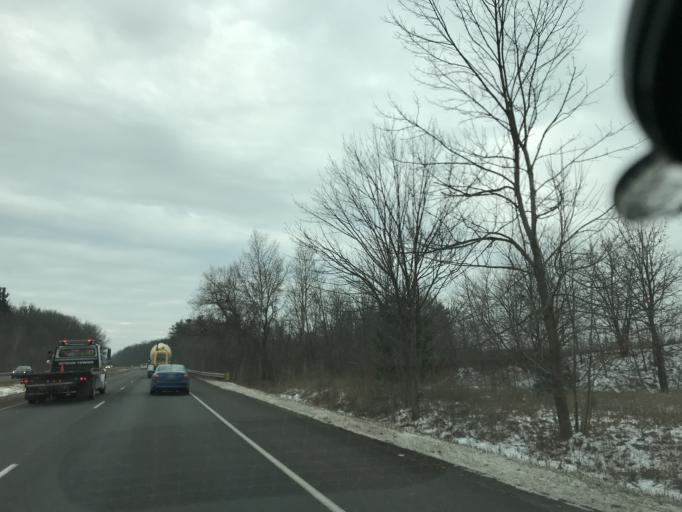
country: US
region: Michigan
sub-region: Kent County
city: Rockford
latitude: 43.1134
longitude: -85.5495
